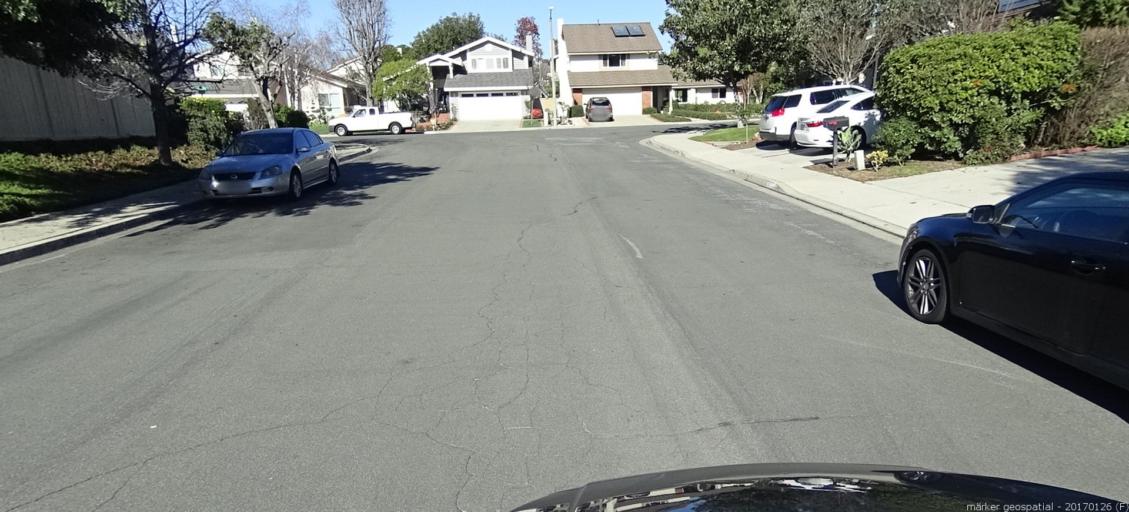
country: US
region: California
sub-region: Orange County
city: Lake Forest
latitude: 33.6311
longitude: -117.6814
